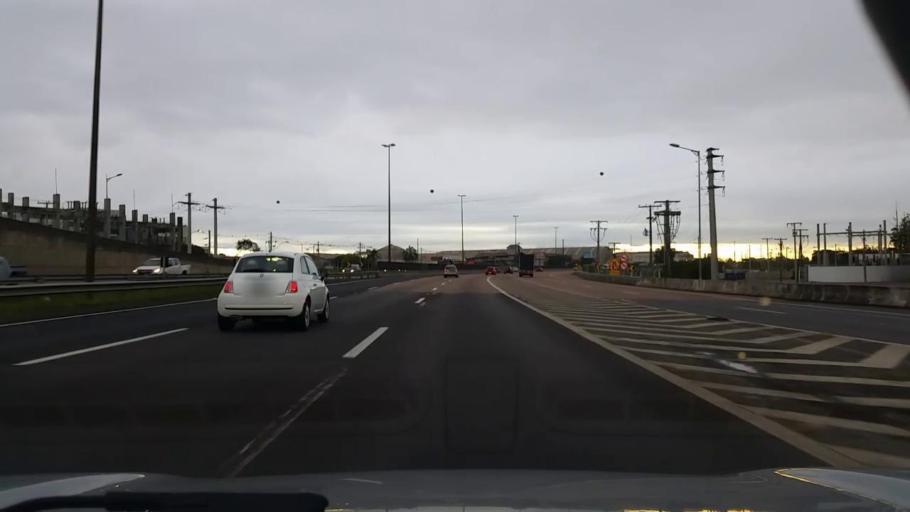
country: BR
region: Rio Grande do Sul
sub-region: Canoas
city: Canoas
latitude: -29.9728
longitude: -51.1965
